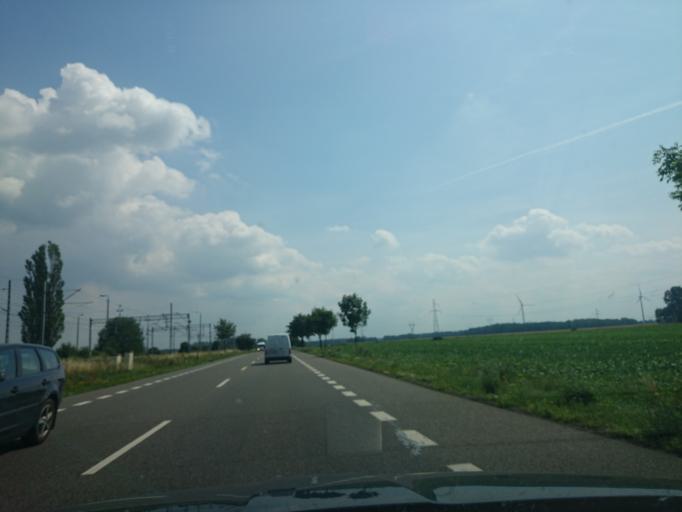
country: PL
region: West Pomeranian Voivodeship
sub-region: Powiat kamienski
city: Wolin
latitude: 53.8452
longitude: 14.6504
